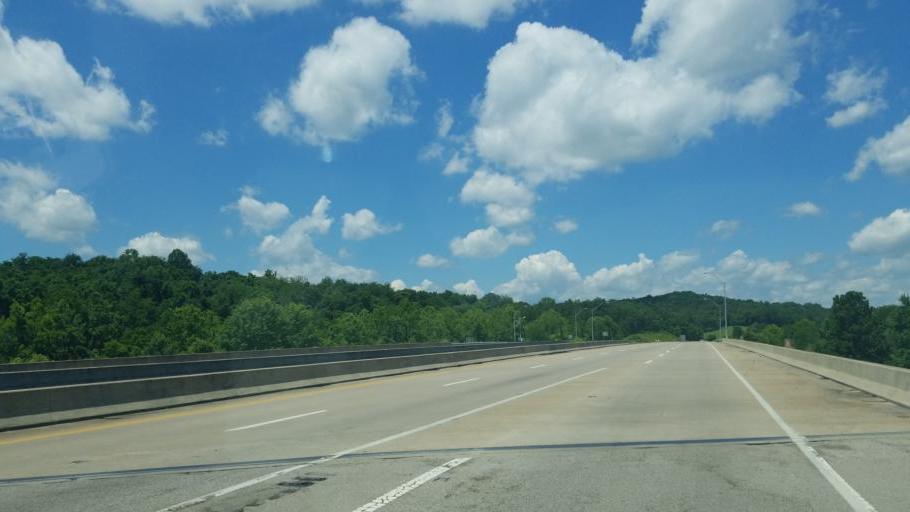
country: US
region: Ohio
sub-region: Gallia County
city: Gallipolis
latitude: 38.8498
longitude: -82.2363
